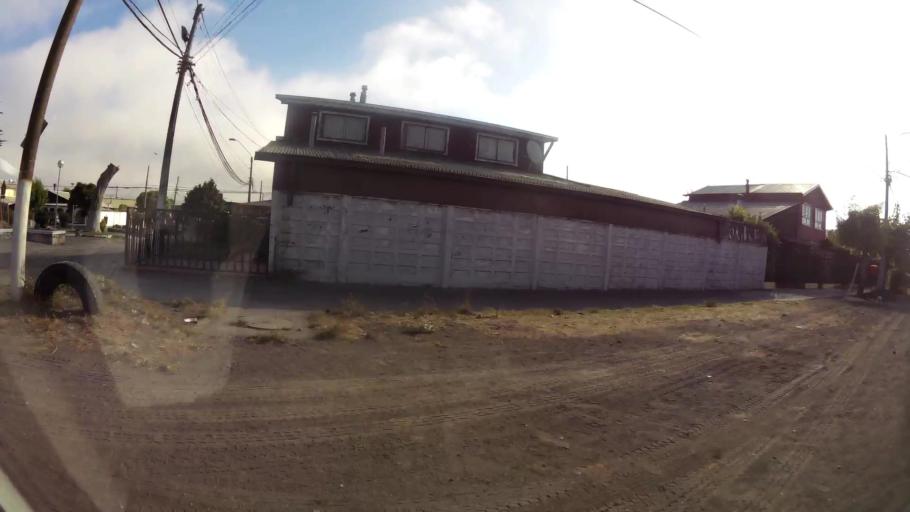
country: CL
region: Biobio
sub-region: Provincia de Concepcion
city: Concepcion
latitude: -36.7932
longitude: -73.0994
